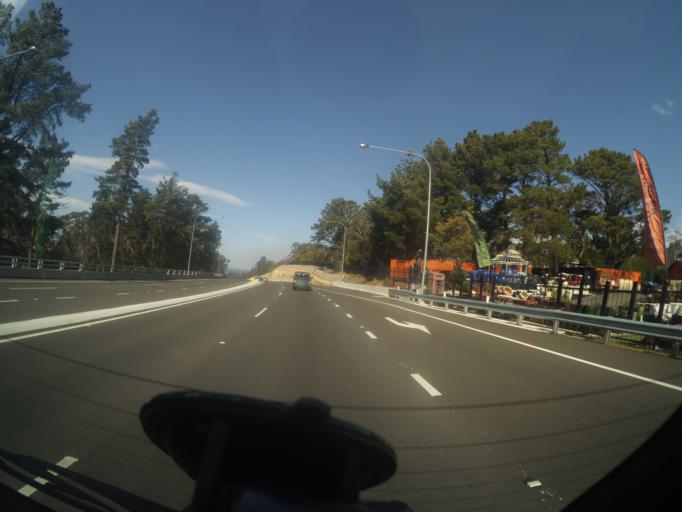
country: AU
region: New South Wales
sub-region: Blue Mountains Municipality
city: Lawson
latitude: -33.7249
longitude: 150.3847
